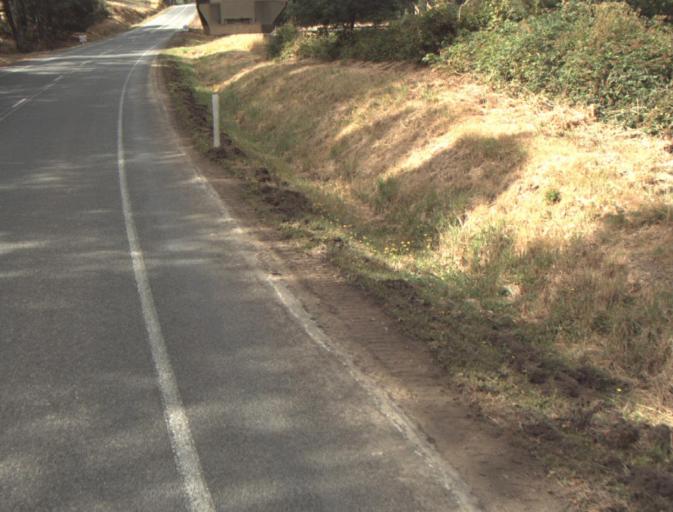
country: AU
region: Tasmania
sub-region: Launceston
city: Mayfield
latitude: -41.2723
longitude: 147.2165
